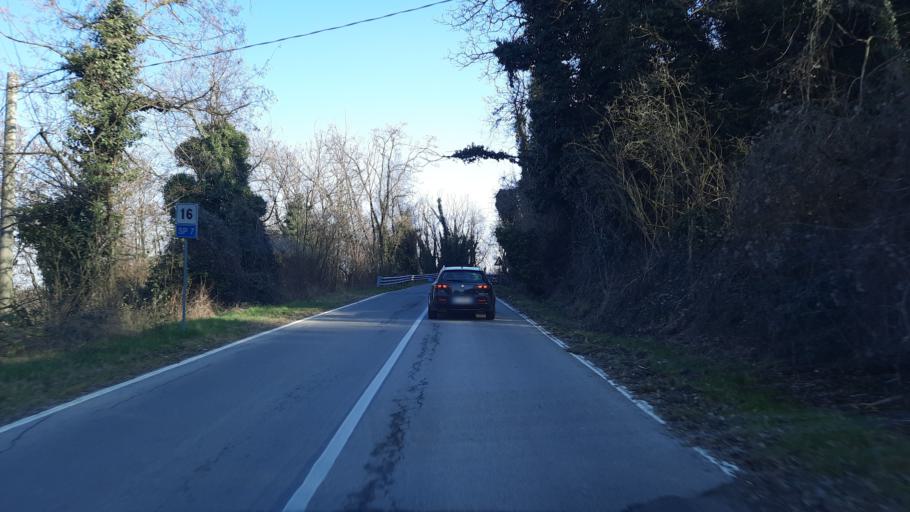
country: IT
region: Piedmont
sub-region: Provincia di Alessandria
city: Camino
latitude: 45.1657
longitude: 8.2902
